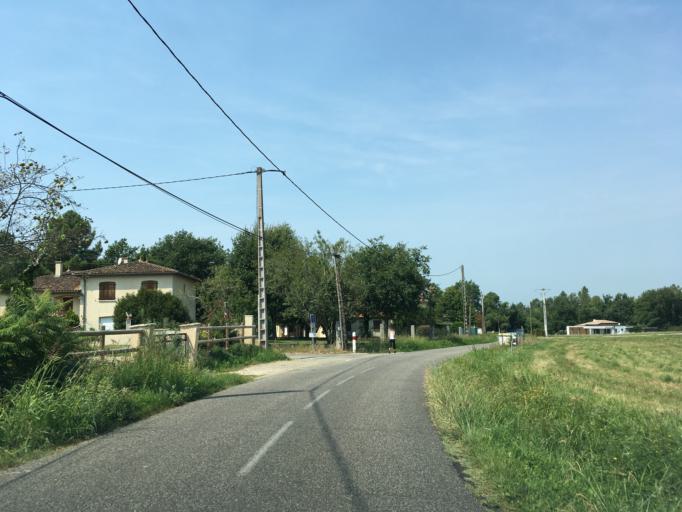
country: FR
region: Midi-Pyrenees
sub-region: Departement du Tarn-et-Garonne
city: Saint-Nauphary
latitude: 43.9899
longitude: 1.4136
